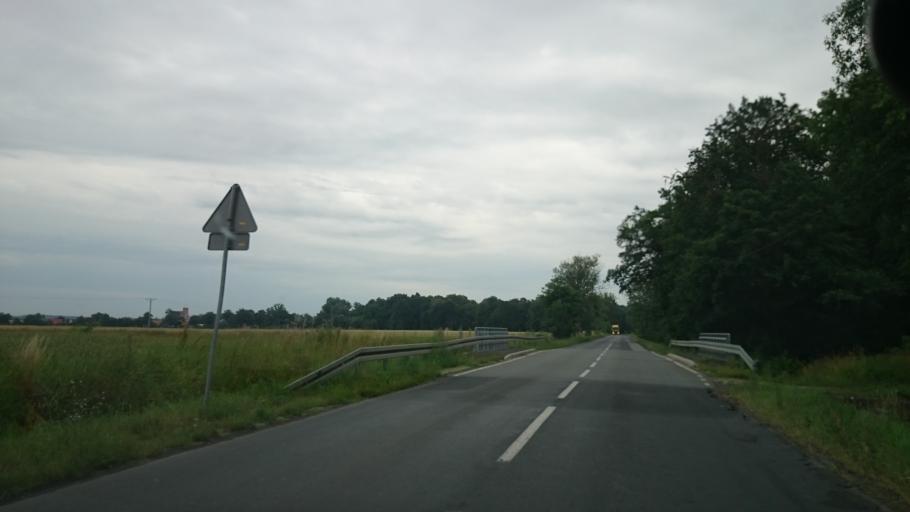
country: PL
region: Opole Voivodeship
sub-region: Powiat brzeski
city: Grodkow
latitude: 50.6537
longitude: 17.4373
